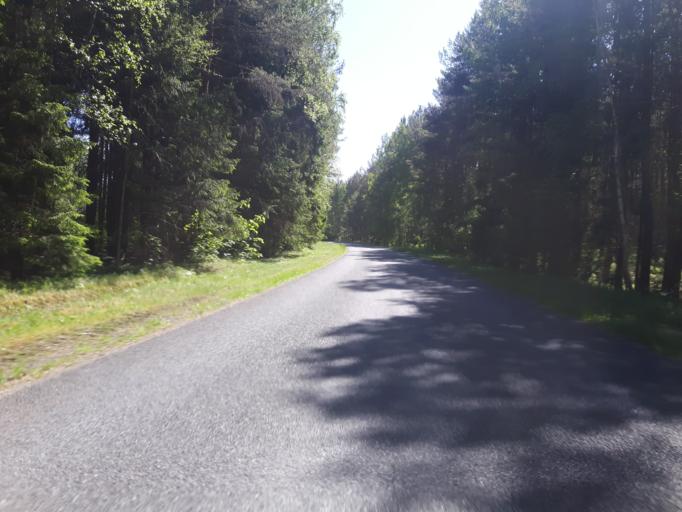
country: EE
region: Laeaene-Virumaa
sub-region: Haljala vald
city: Haljala
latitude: 59.5642
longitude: 26.2388
